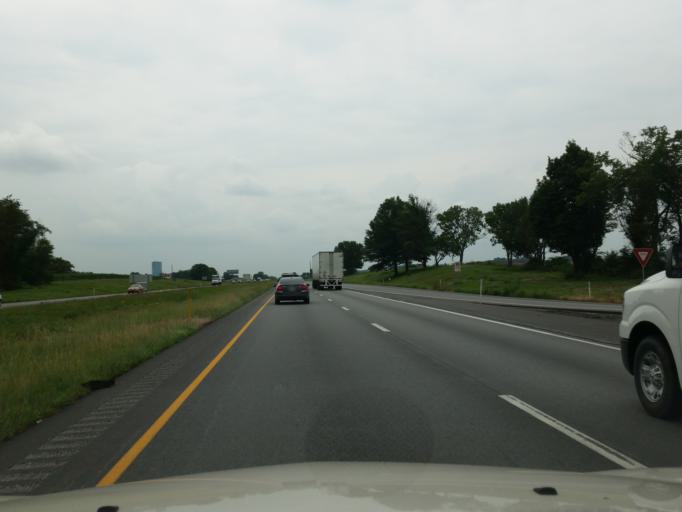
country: US
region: Pennsylvania
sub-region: Lancaster County
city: Salunga
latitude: 40.1166
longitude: -76.4530
